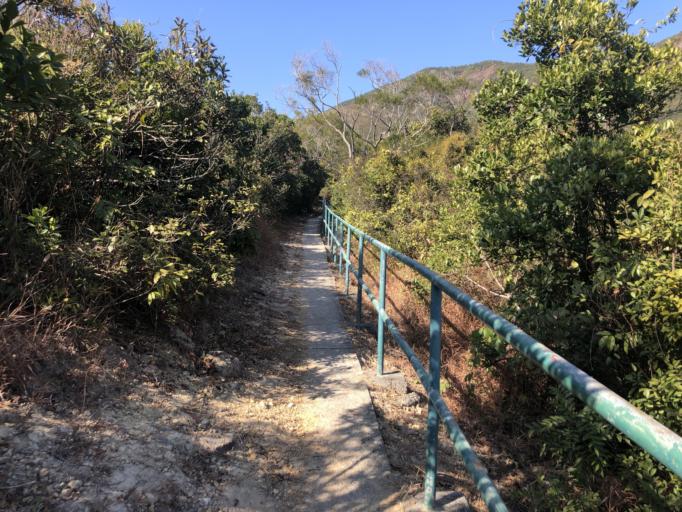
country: HK
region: Wanchai
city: Wan Chai
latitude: 22.2229
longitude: 114.2043
